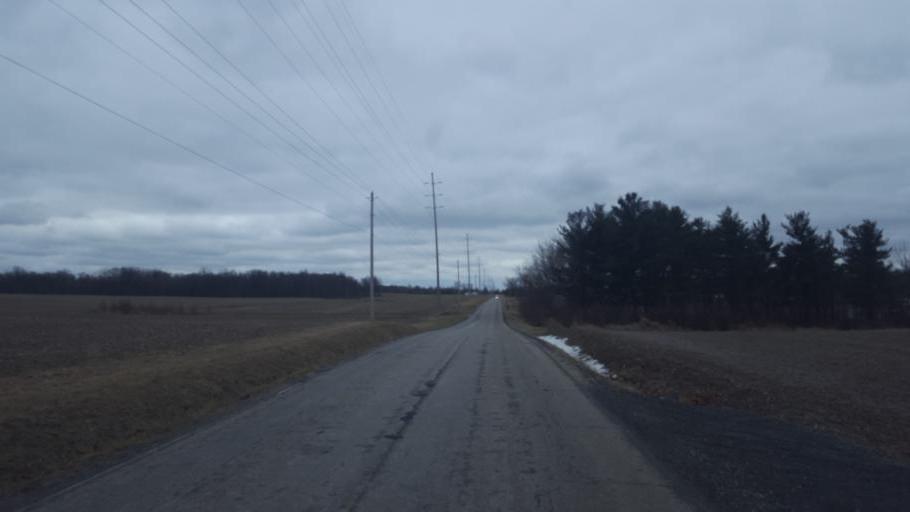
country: US
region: Ohio
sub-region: Crawford County
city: Crestline
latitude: 40.7843
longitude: -82.6976
